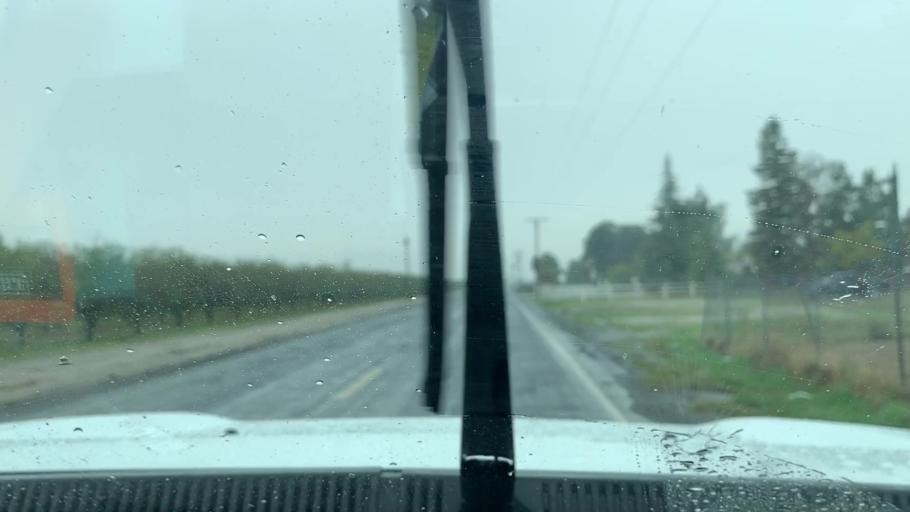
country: US
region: California
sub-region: Tulare County
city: Earlimart
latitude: 35.8919
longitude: -119.3275
